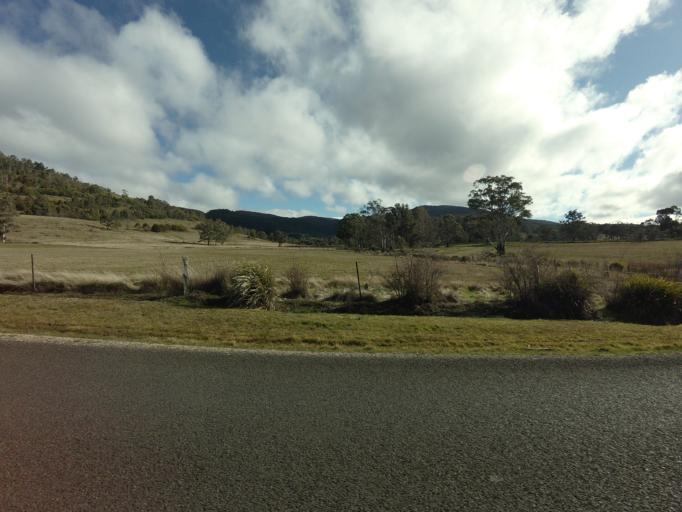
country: AU
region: Tasmania
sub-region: Derwent Valley
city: New Norfolk
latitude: -42.6059
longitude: 146.7058
